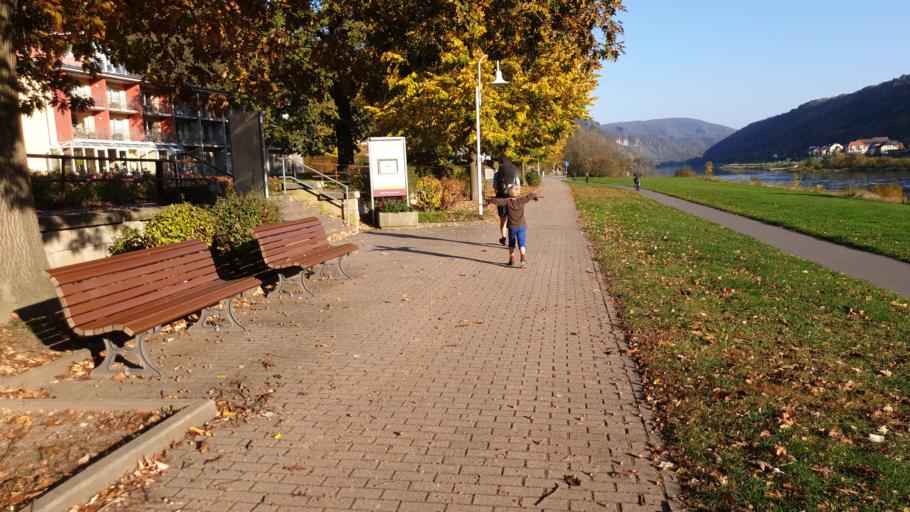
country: DE
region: Saxony
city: Bad Schandau
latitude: 50.9153
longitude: 14.1610
